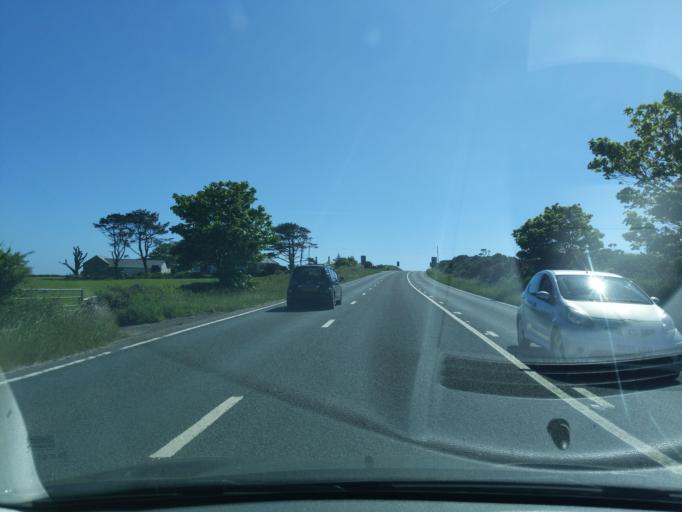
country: GB
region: England
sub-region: Cornwall
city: Wendron
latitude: 50.1446
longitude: -5.2142
